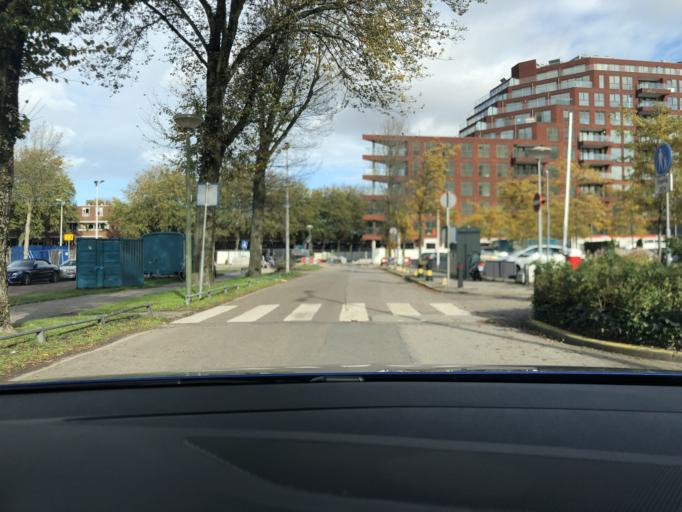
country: NL
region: South Holland
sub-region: Gemeente Den Haag
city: The Hague
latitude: 52.0561
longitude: 4.2619
